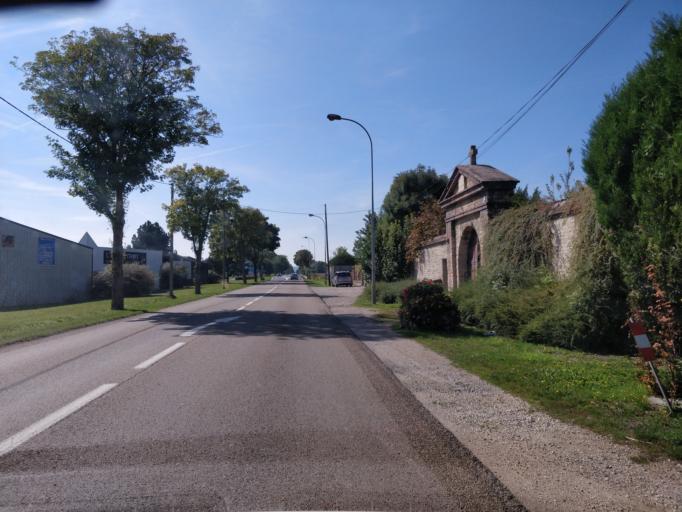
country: FR
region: Champagne-Ardenne
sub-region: Departement de l'Aube
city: Saint-Germain
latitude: 48.2542
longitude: 4.0283
